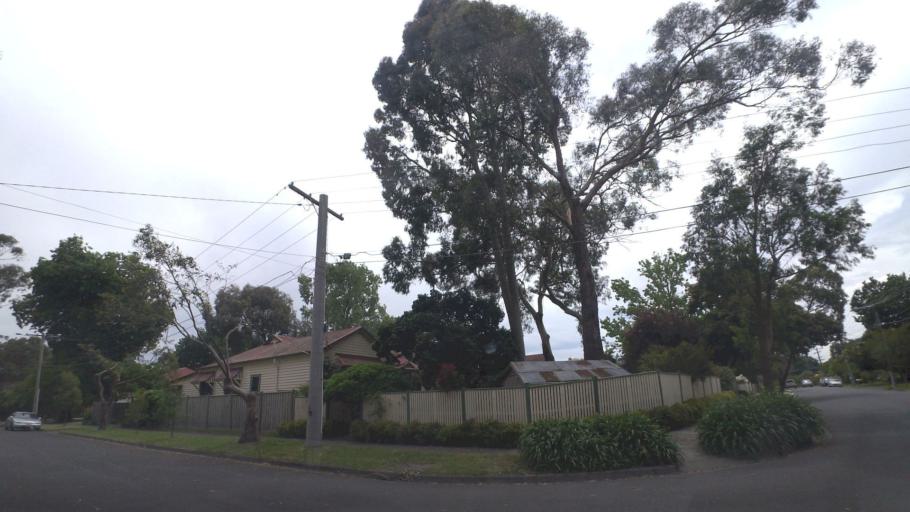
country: AU
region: Victoria
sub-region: Yarra Ranges
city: Kilsyth
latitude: -37.8046
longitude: 145.3007
